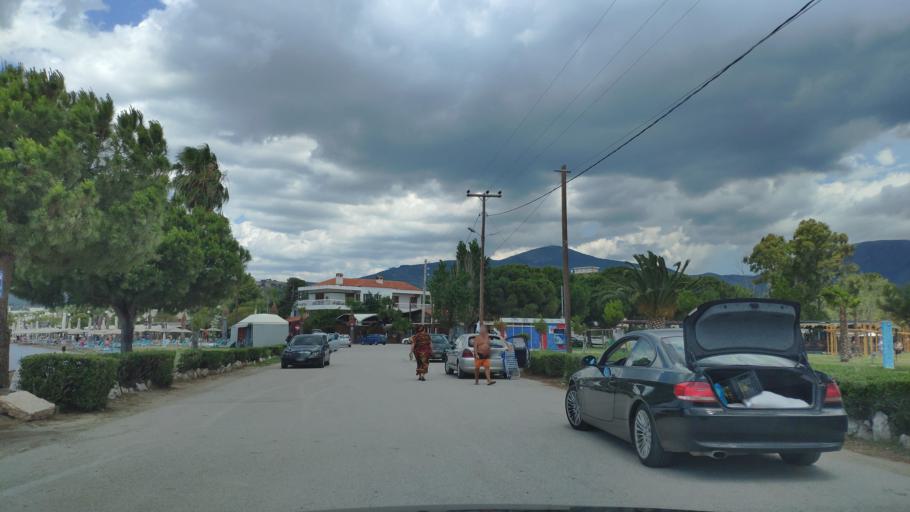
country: GR
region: Central Greece
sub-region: Nomos Evvoias
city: Eretria
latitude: 38.3876
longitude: 23.8004
